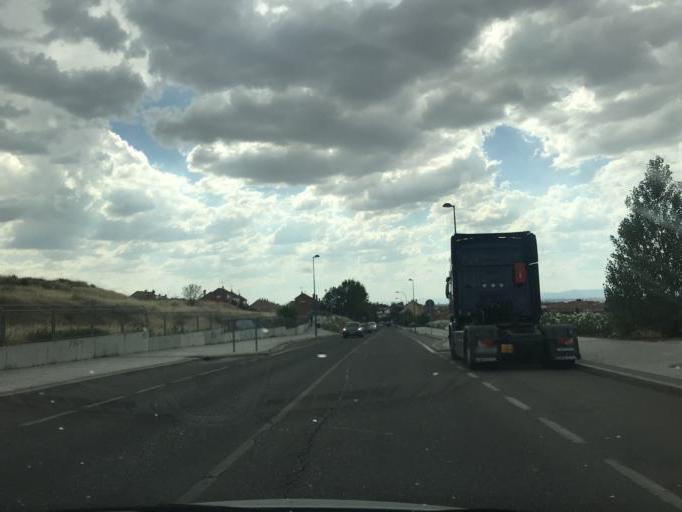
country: ES
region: Madrid
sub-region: Provincia de Madrid
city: Paracuellos de Jarama
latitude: 40.5054
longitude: -3.5225
